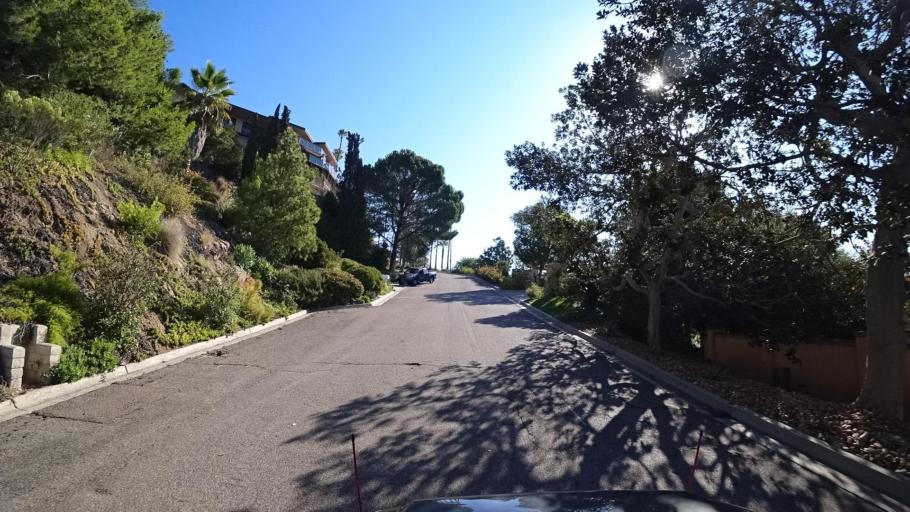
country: US
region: California
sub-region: San Diego County
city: Casa de Oro-Mount Helix
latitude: 32.7647
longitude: -116.9831
